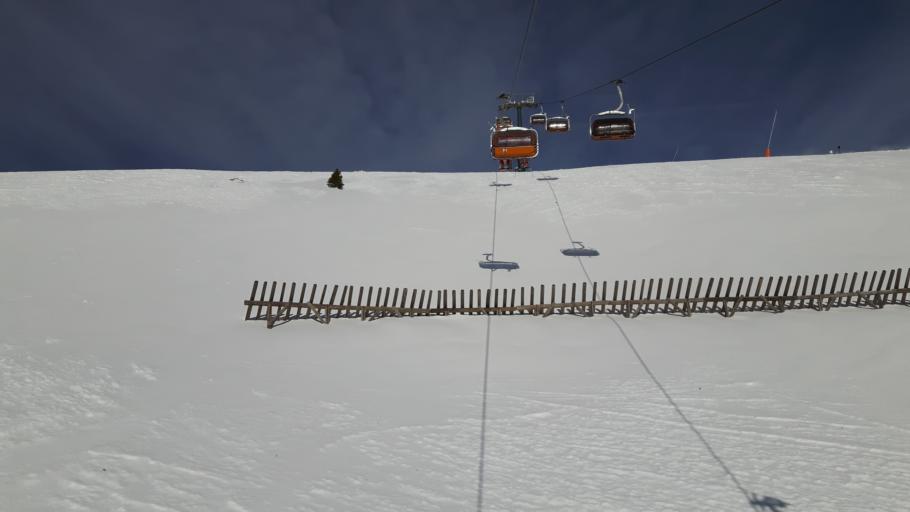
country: IT
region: Trentino-Alto Adige
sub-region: Provincia di Trento
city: Moena
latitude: 46.3410
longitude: 11.6958
